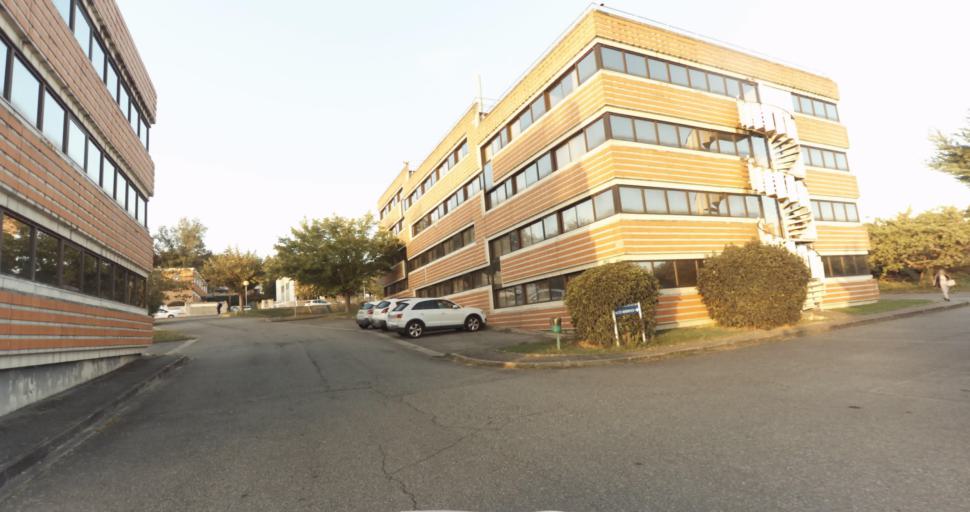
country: FR
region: Midi-Pyrenees
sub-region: Departement de la Haute-Garonne
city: Auzeville-Tolosane
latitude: 43.5374
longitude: 1.4807
